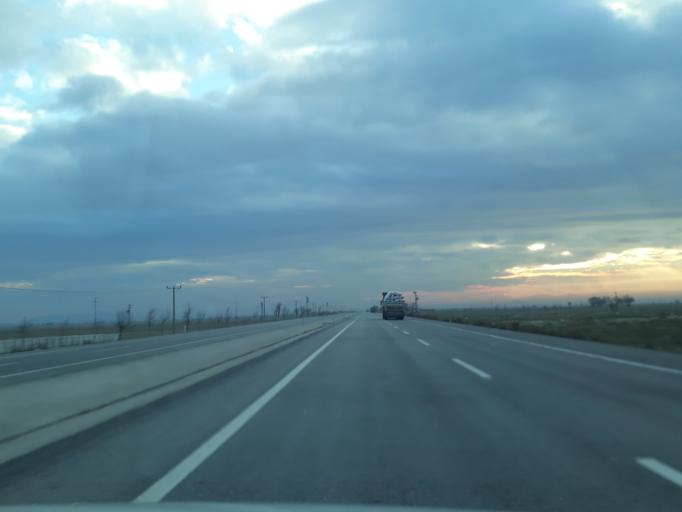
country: TR
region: Konya
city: Hotamis
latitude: 37.7108
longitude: 33.2899
